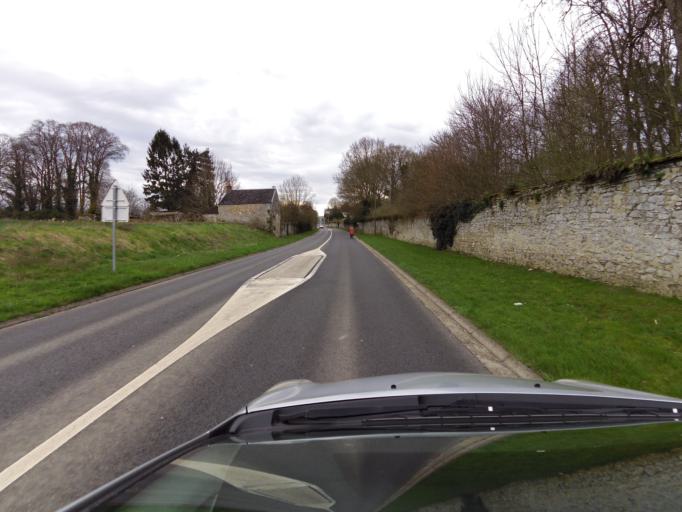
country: FR
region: Picardie
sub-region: Departement de l'Oise
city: Chamant
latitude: 49.1966
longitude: 2.6239
